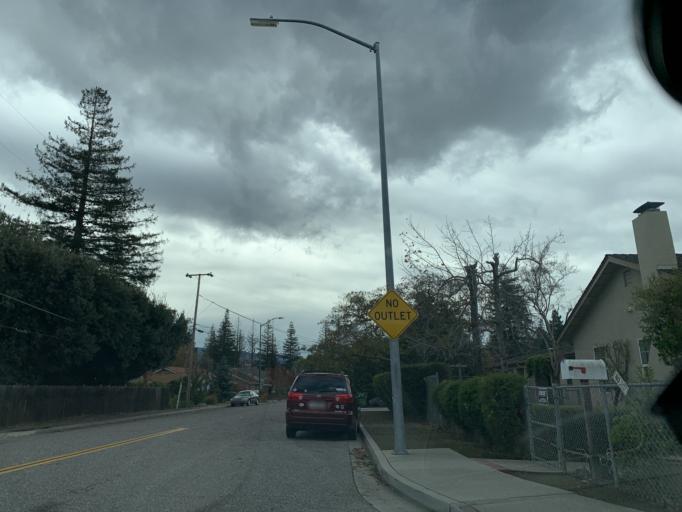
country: US
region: California
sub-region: Santa Clara County
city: Campbell
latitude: 37.2773
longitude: -121.9722
